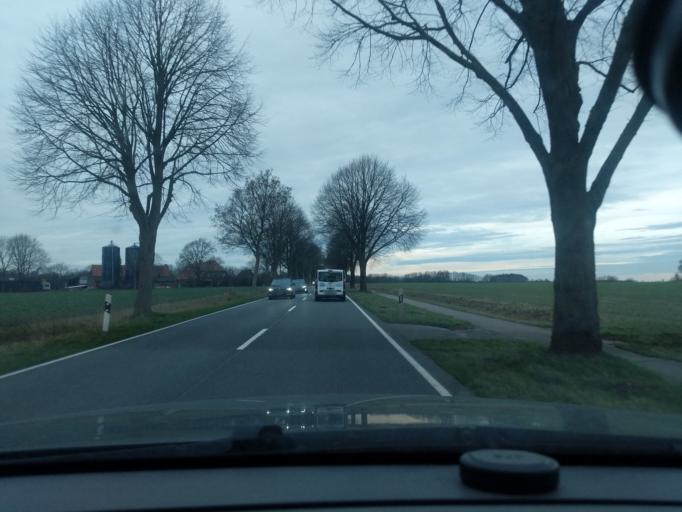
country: DE
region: Lower Saxony
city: Beckdorf
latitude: 53.4011
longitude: 9.6102
